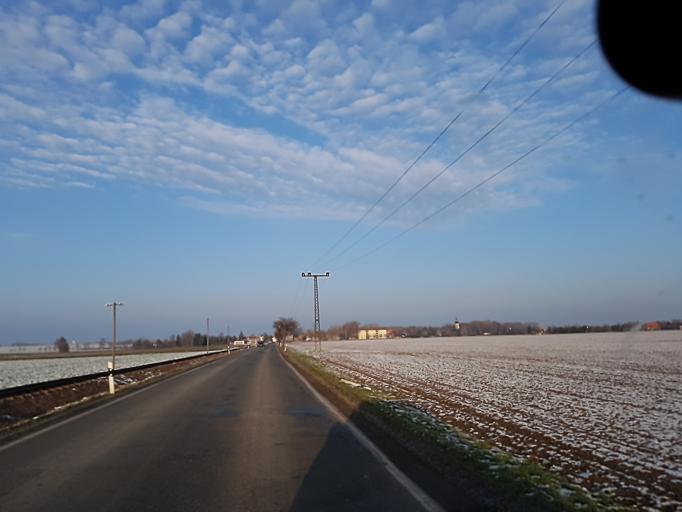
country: DE
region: Saxony
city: Naundorf
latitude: 51.2533
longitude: 13.0950
